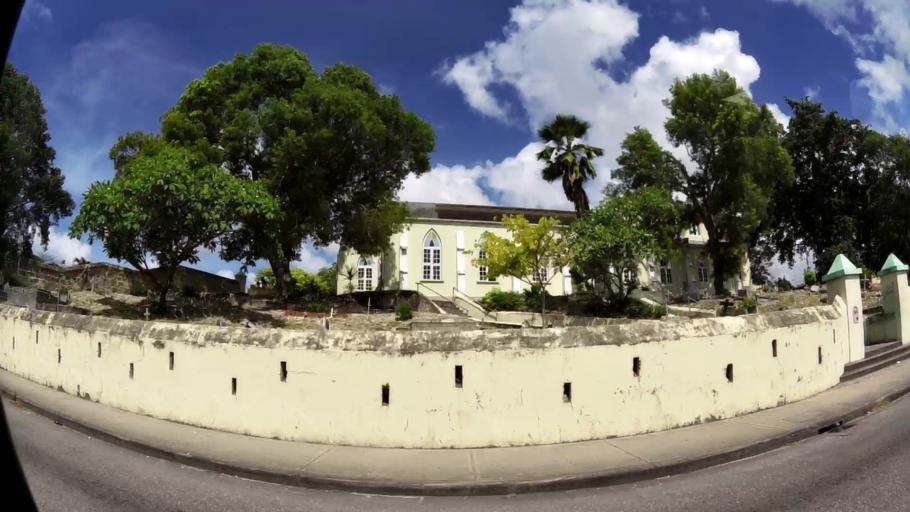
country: BB
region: Saint Michael
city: Bridgetown
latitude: 13.1257
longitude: -59.6260
